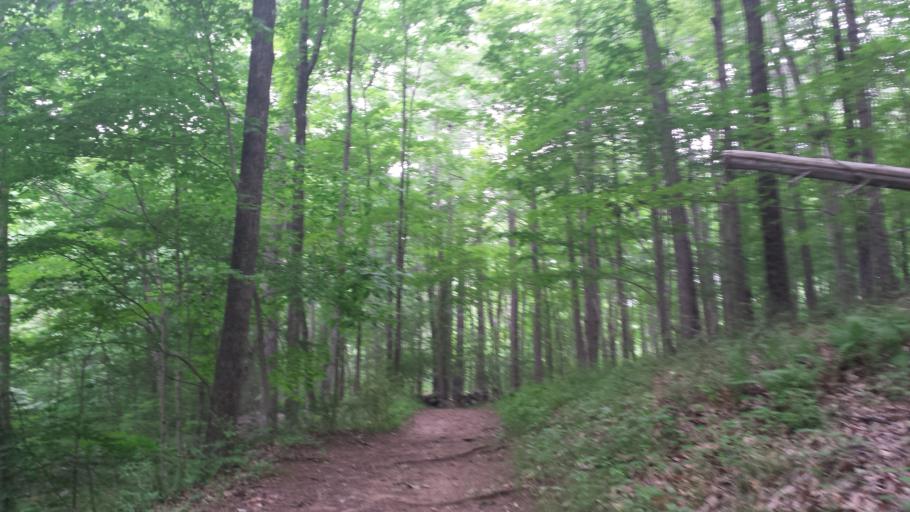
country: US
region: New York
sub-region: Westchester County
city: Pound Ridge
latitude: 41.2630
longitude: -73.5914
